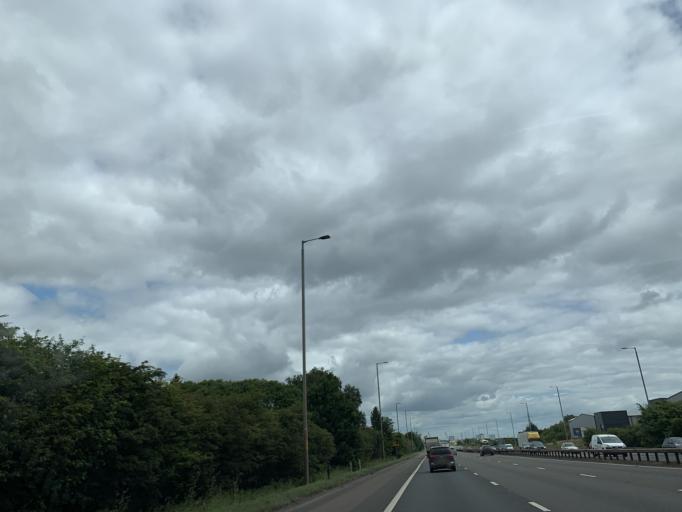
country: GB
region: Scotland
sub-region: Renfrewshire
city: Renfrew
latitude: 55.8649
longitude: -4.3823
